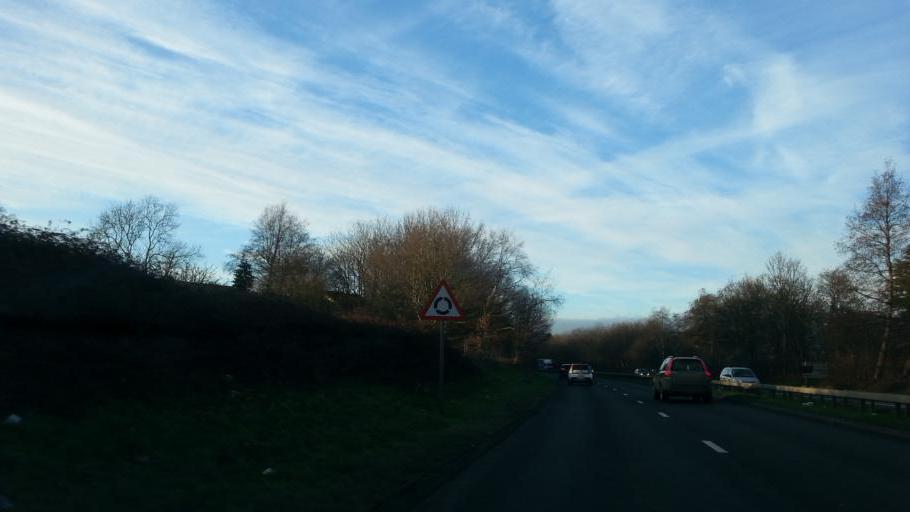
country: GB
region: England
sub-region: Northamptonshire
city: Hardingstone
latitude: 52.2224
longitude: -0.9198
